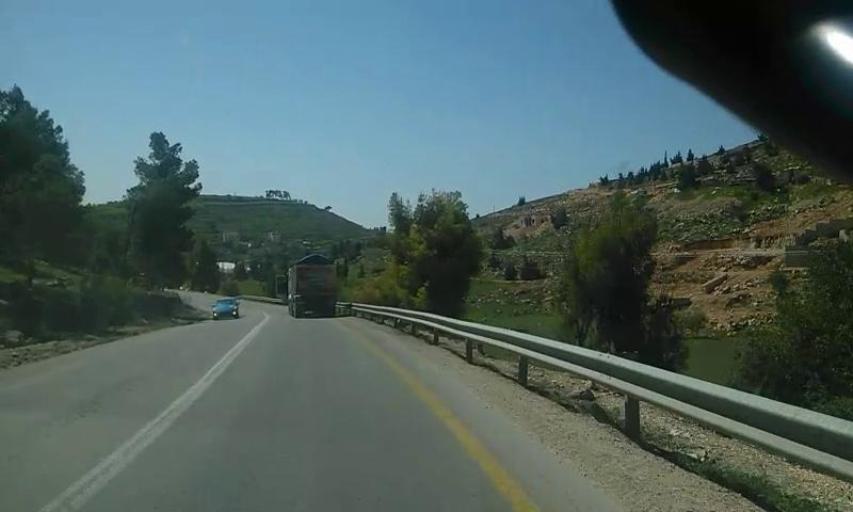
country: PS
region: West Bank
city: Ar Rihiyah
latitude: 31.4896
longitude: 35.0659
